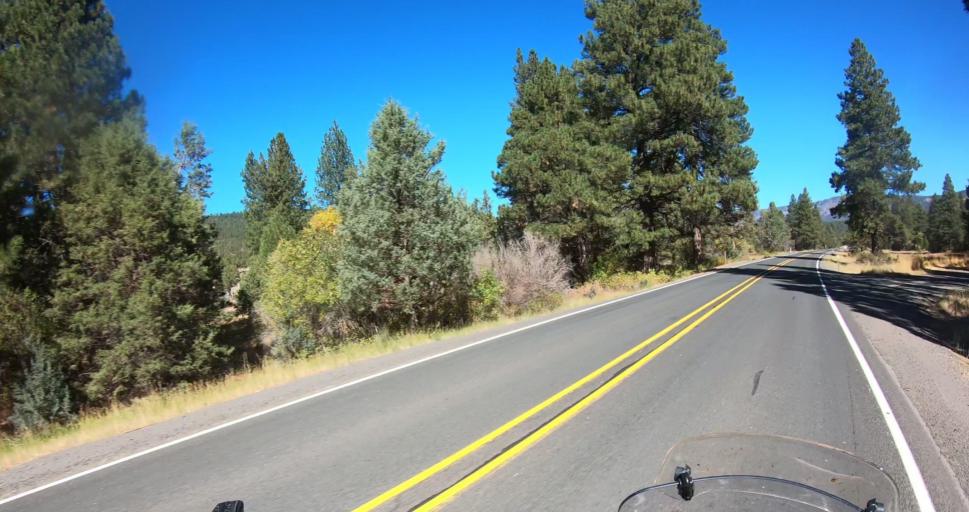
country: US
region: Oregon
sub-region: Lake County
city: Lakeview
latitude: 42.3930
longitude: -120.3001
